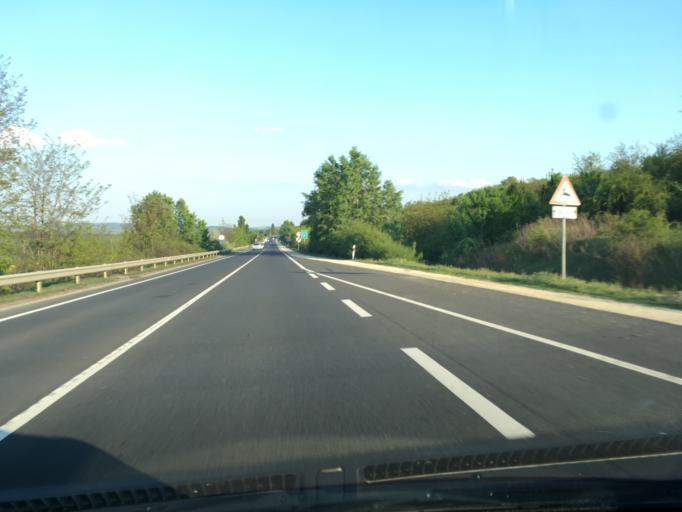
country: HU
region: Pest
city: Kosd
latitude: 47.7900
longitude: 19.1597
